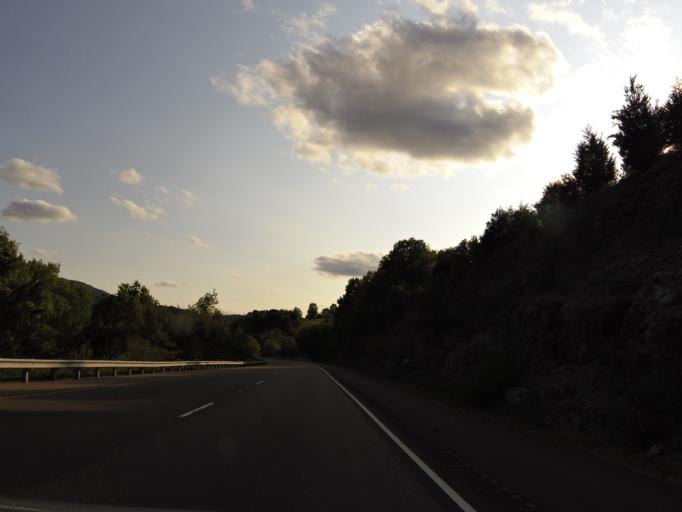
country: US
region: Virginia
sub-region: Tazewell County
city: Raven
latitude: 36.9915
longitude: -81.8427
